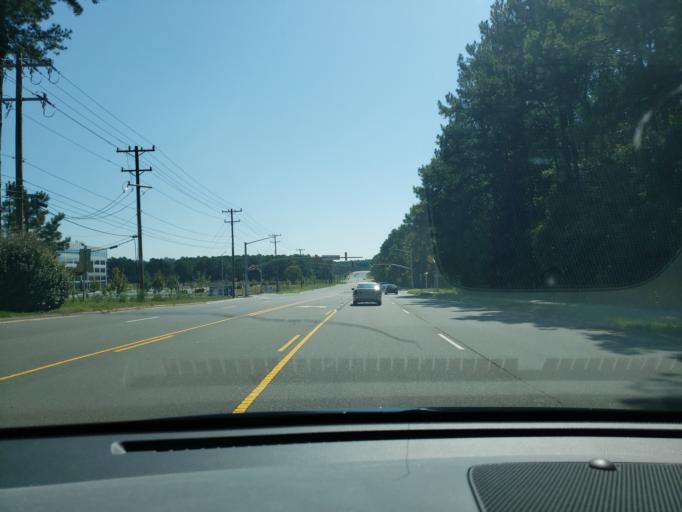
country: US
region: North Carolina
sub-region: Durham County
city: Durham
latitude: 35.9003
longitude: -78.8856
